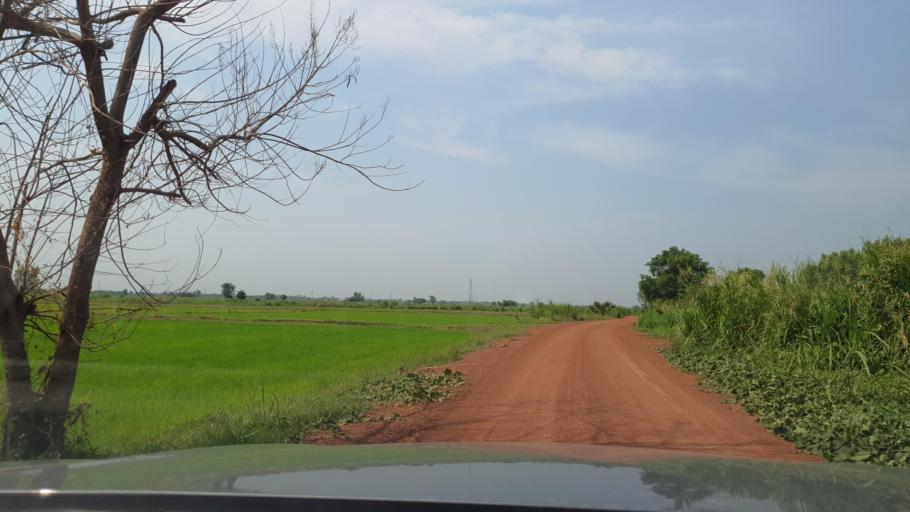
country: TH
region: Phitsanulok
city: Bang Rakam
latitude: 16.7906
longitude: 100.1095
